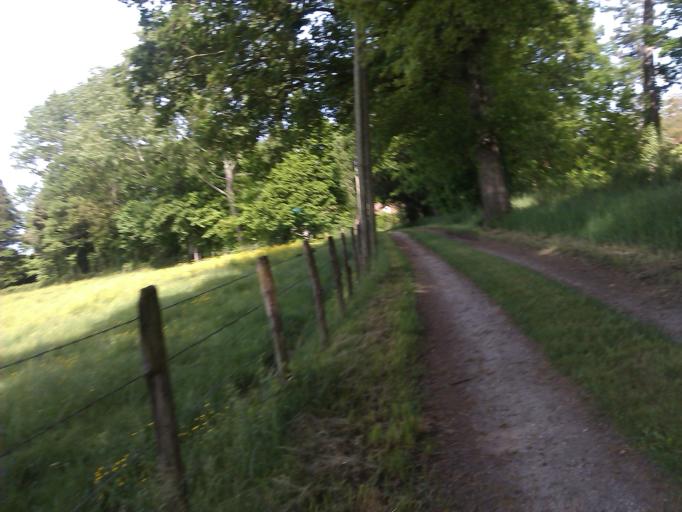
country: FR
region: Auvergne
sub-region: Departement de l'Allier
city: Dompierre-sur-Besbre
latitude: 46.5317
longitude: 3.6748
